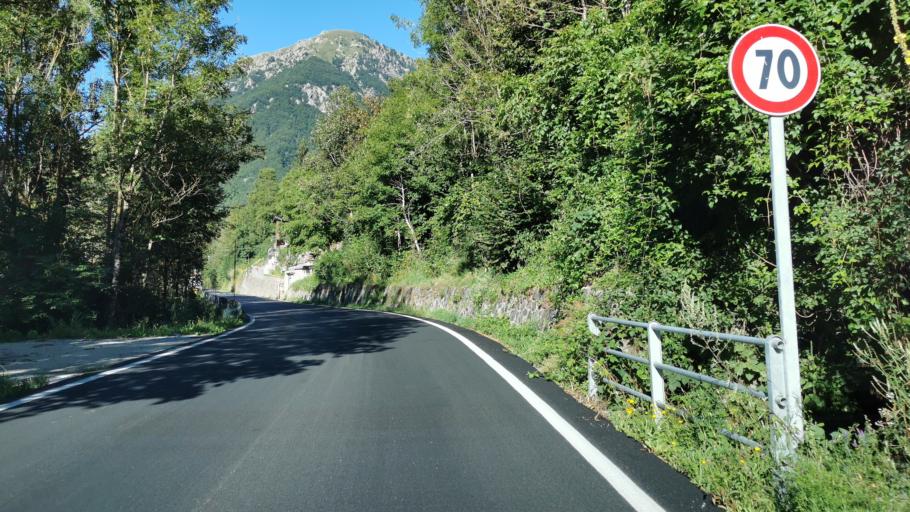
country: IT
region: Piedmont
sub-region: Provincia di Cuneo
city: Entracque
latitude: 44.2499
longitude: 7.3347
